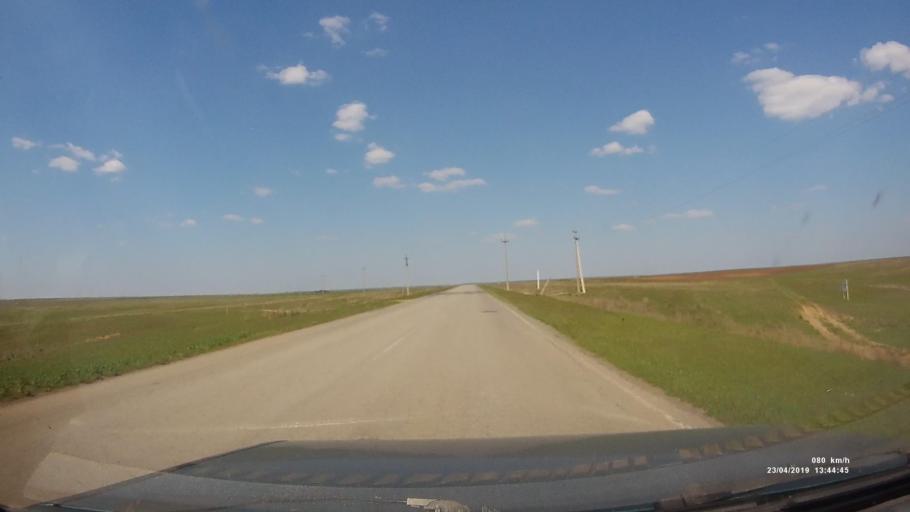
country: RU
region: Kalmykiya
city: Yashalta
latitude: 46.5846
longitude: 42.8180
